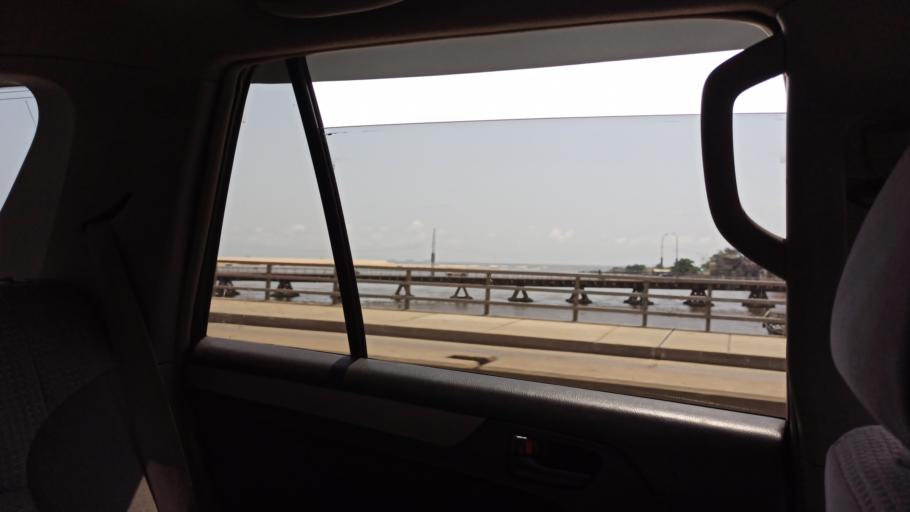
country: BJ
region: Littoral
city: Cotonou
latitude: 6.3595
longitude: 2.4407
